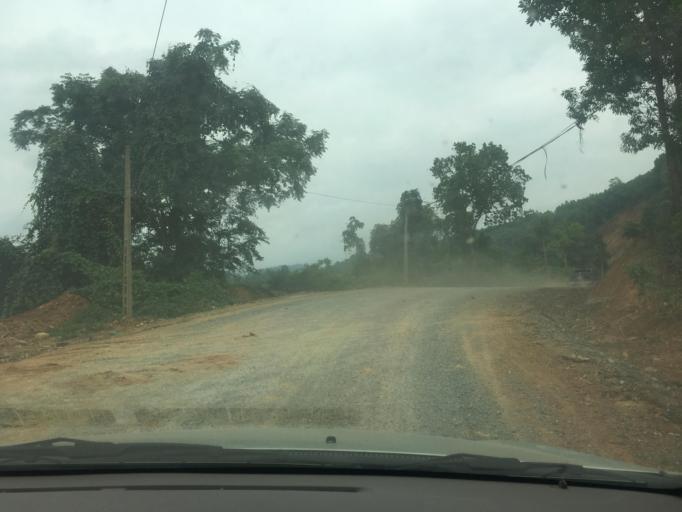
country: VN
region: Lang Son
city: Binh Gia
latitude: 22.1293
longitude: 106.3514
